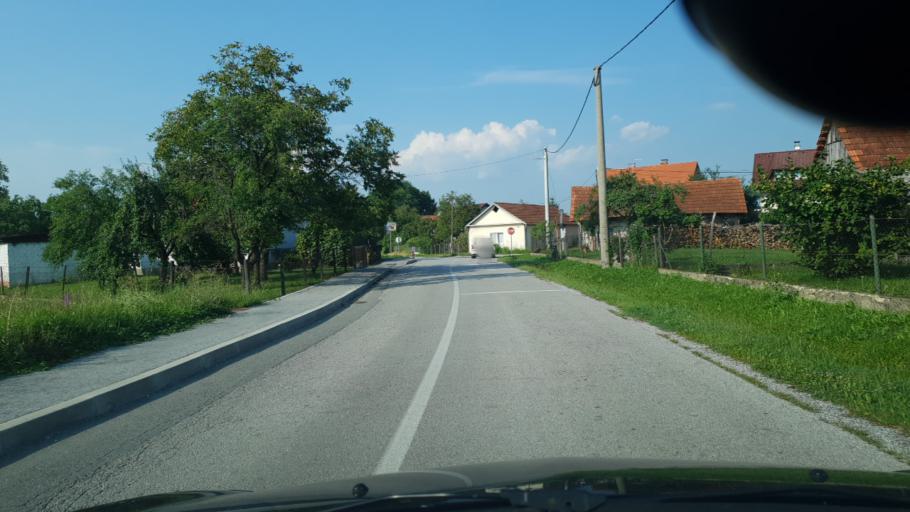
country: HR
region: Krapinsko-Zagorska
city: Oroslavje
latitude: 45.9827
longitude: 15.9227
